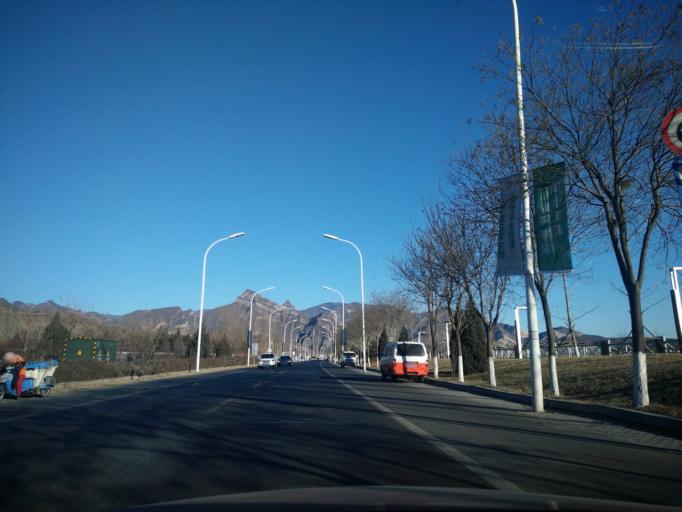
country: CN
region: Beijing
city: Junzhuang
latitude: 39.9786
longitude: 116.0835
